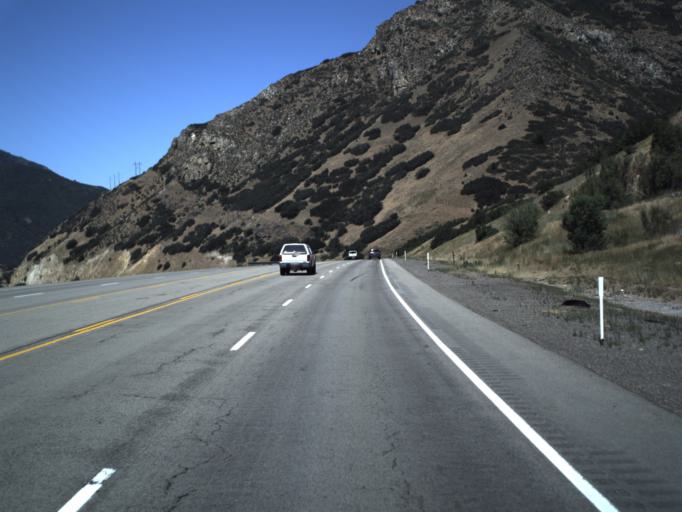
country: US
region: Utah
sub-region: Utah County
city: Mapleton
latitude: 40.0310
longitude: -111.5121
